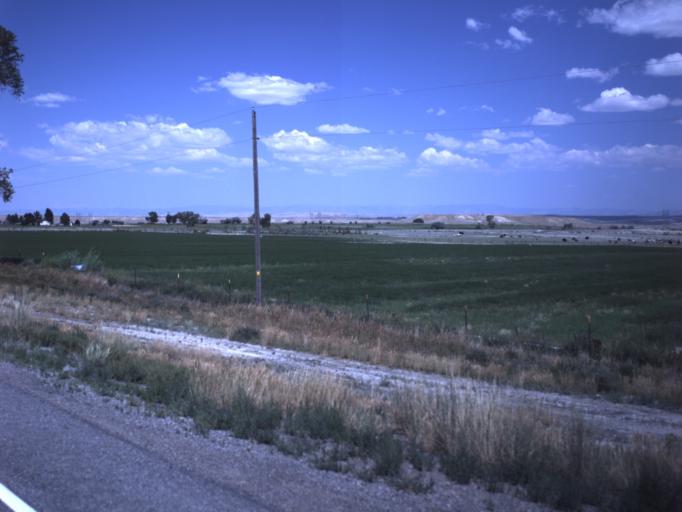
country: US
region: Utah
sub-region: Emery County
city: Castle Dale
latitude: 39.2402
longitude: -110.9903
